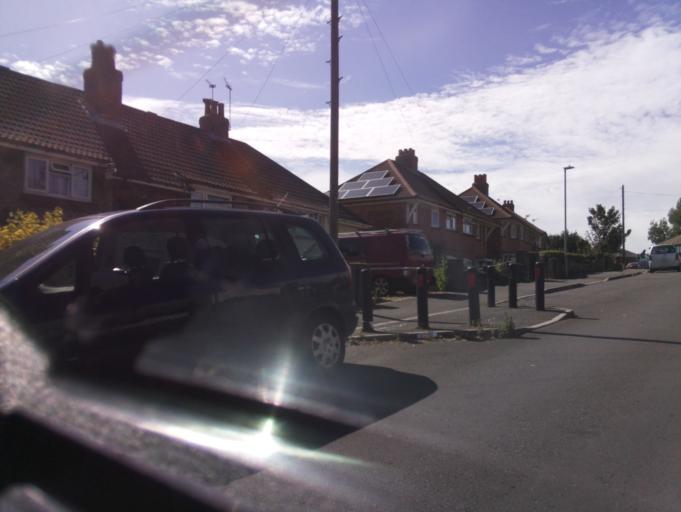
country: GB
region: England
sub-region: Dorset
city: Parkstone
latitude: 50.7372
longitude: -1.9482
